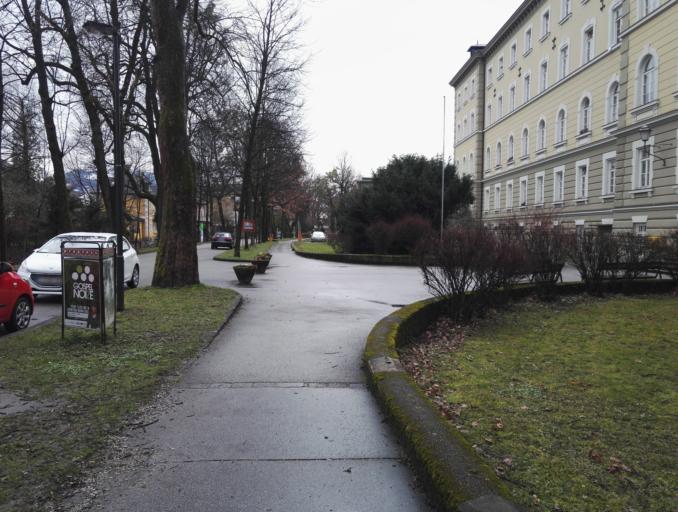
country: AT
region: Salzburg
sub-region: Salzburg Stadt
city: Salzburg
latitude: 47.7908
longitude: 13.0602
